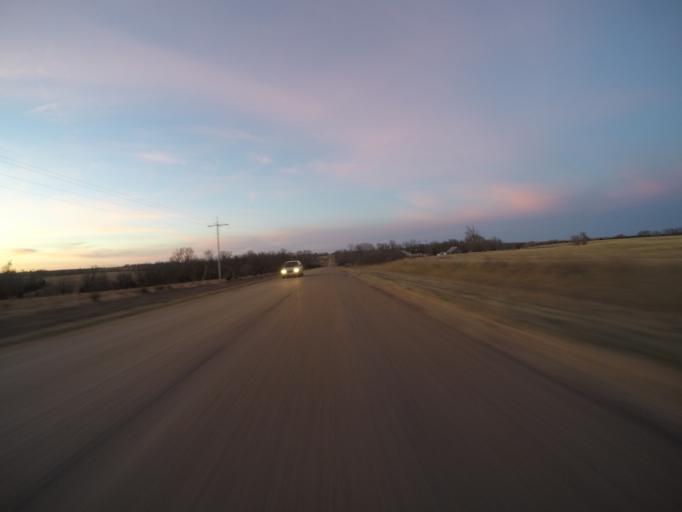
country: US
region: Kansas
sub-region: Washington County
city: Washington
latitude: 39.7606
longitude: -96.9753
